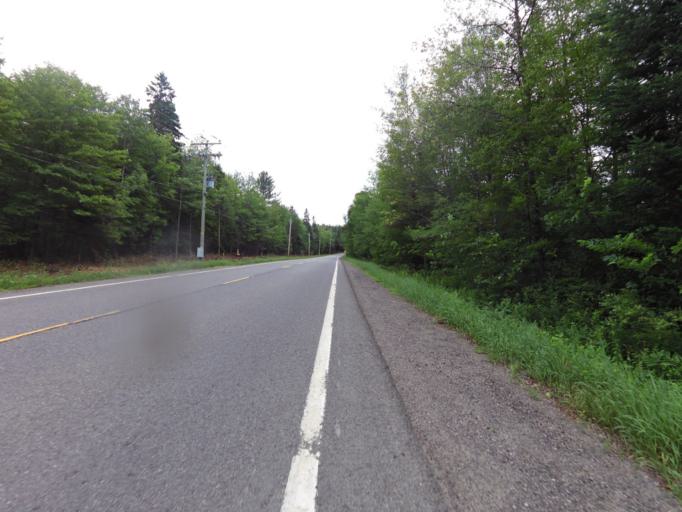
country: CA
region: Quebec
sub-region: Laurentides
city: Brownsburg-Chatham
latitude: 45.8634
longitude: -74.5642
